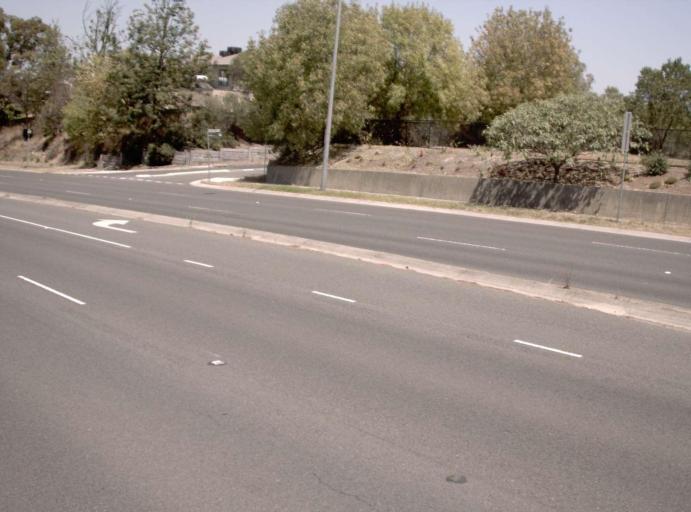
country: AU
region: Victoria
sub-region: Manningham
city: Donvale
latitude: -37.8013
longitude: 145.1783
